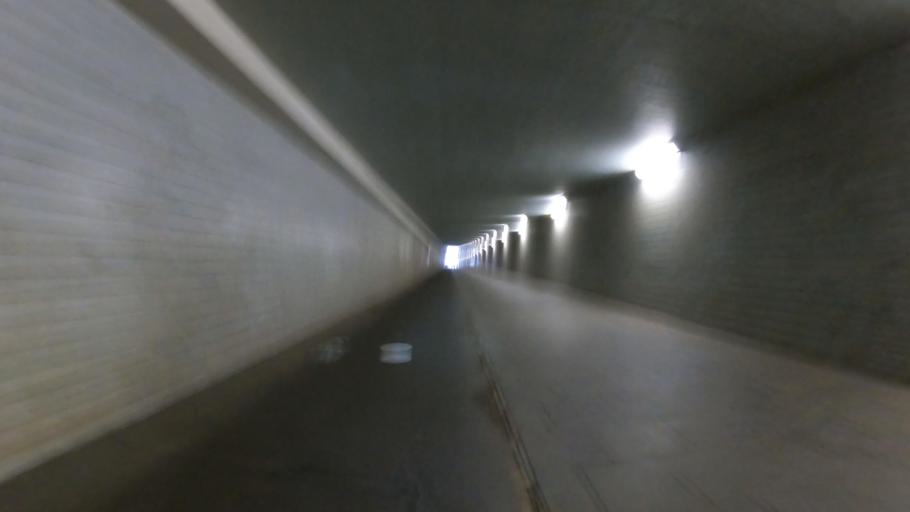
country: DE
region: Hamburg
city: Langenhorn
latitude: 53.6507
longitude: 9.9797
